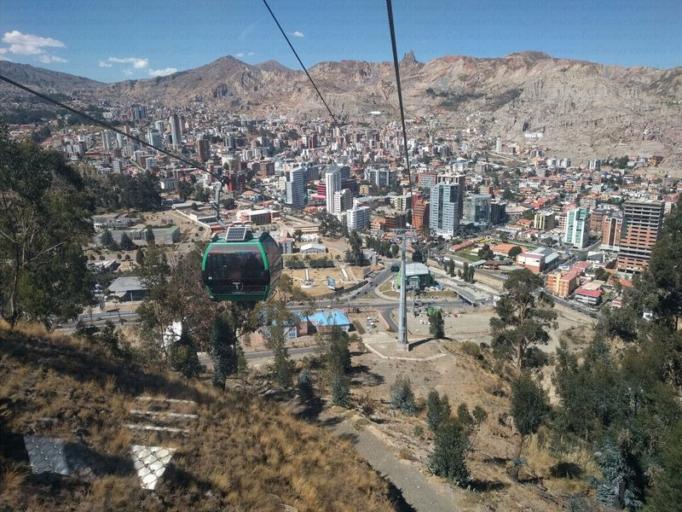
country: BO
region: La Paz
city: La Paz
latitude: -16.5334
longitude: -68.0932
